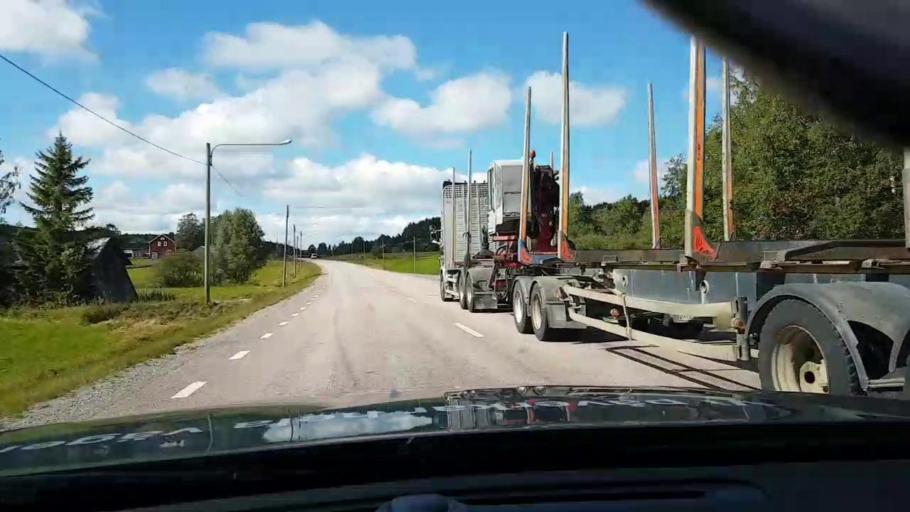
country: SE
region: Vaesternorrland
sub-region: OErnskoeldsviks Kommun
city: Bjasta
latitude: 63.3853
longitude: 18.3875
